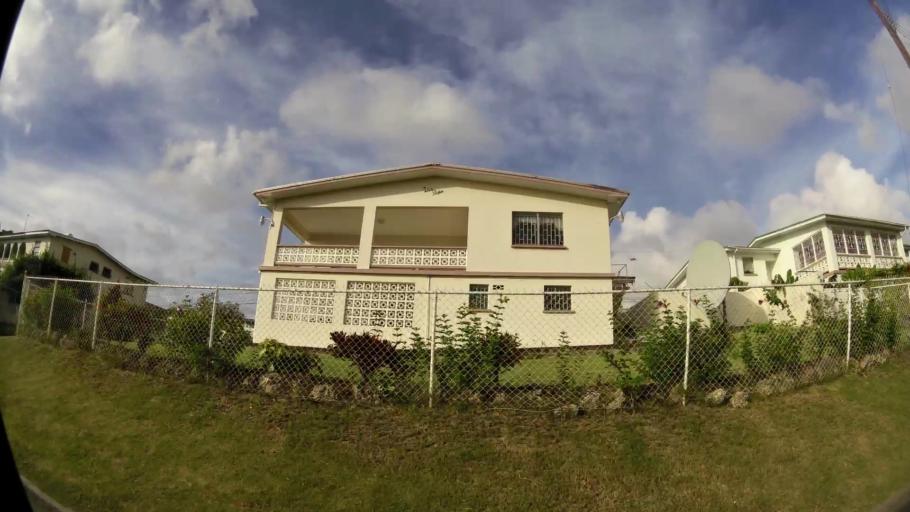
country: BB
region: Christ Church
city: Oistins
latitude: 13.0881
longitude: -59.5713
